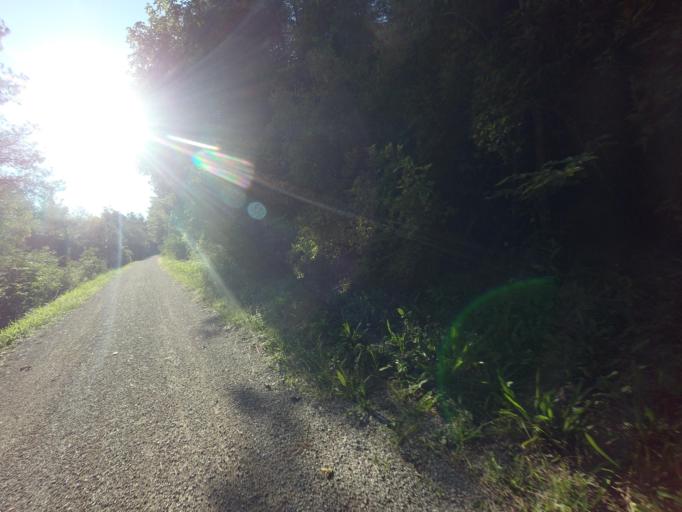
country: CA
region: Ontario
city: Goderich
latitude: 43.7515
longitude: -81.5812
